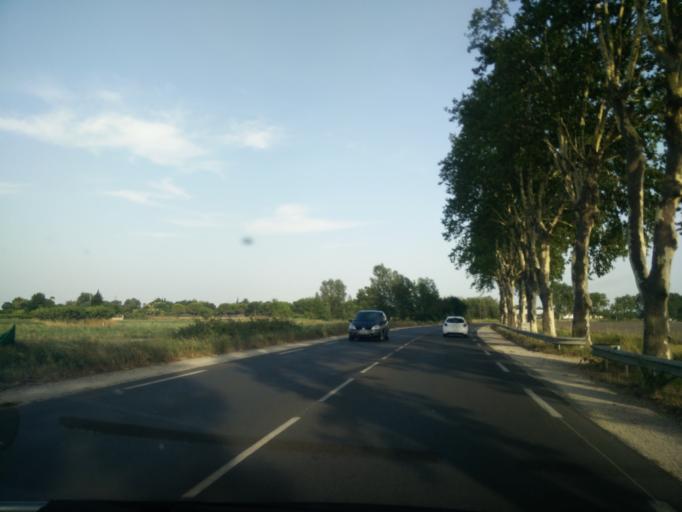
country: FR
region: Languedoc-Roussillon
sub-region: Departement de l'Herault
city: Marsillargues
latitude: 43.6683
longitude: 4.1568
